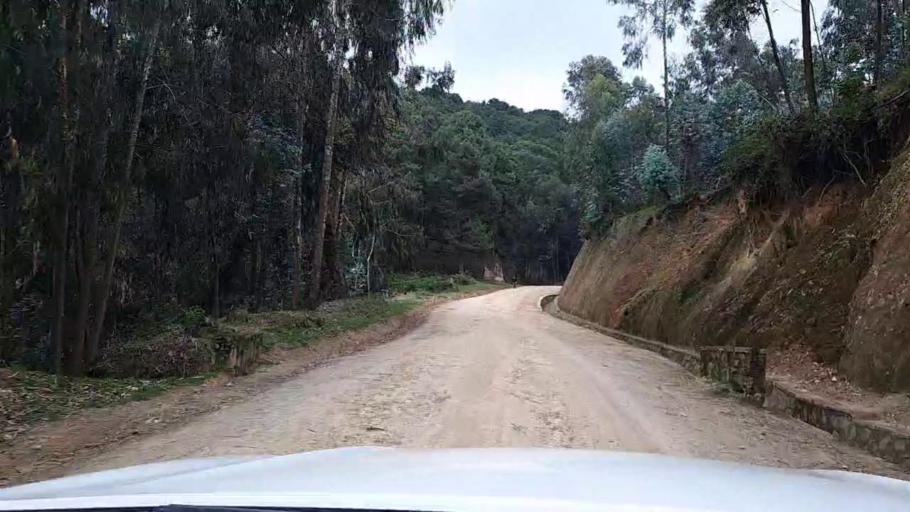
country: RW
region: Southern Province
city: Nzega
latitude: -2.3822
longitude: 29.3838
